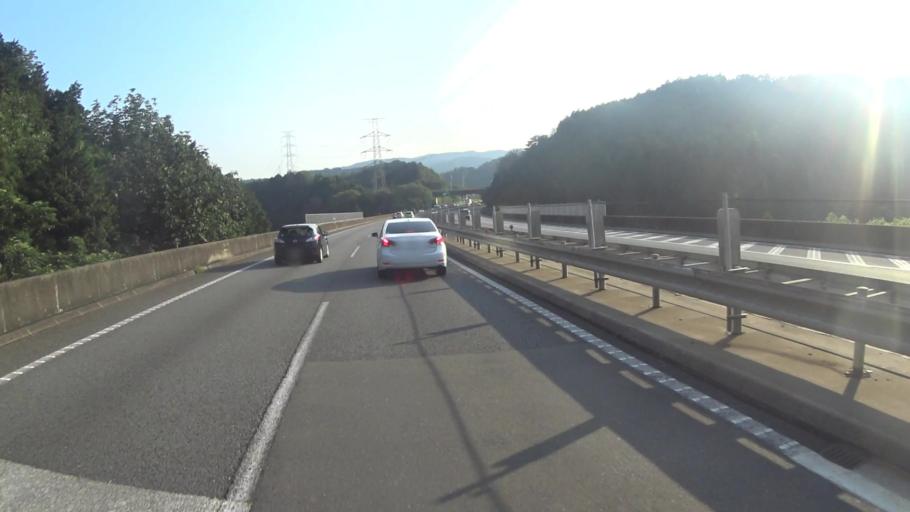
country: JP
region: Shiga Prefecture
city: Otsu-shi
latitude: 34.9234
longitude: 135.8861
